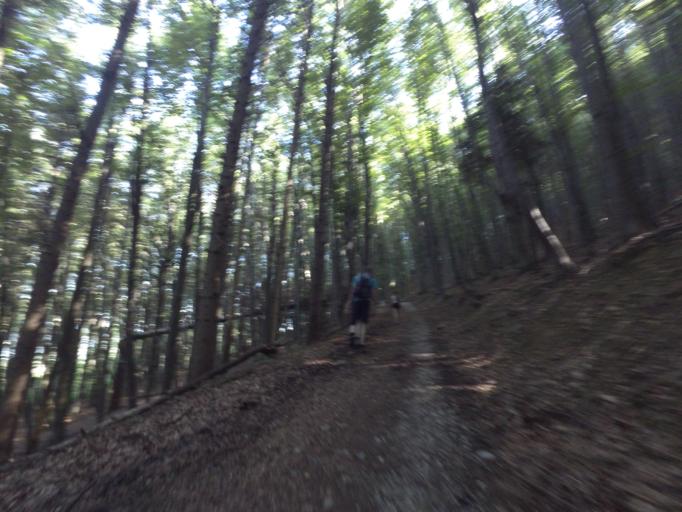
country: AT
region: Salzburg
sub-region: Politischer Bezirk Salzburg-Umgebung
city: Mattsee
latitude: 47.9528
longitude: 13.1063
